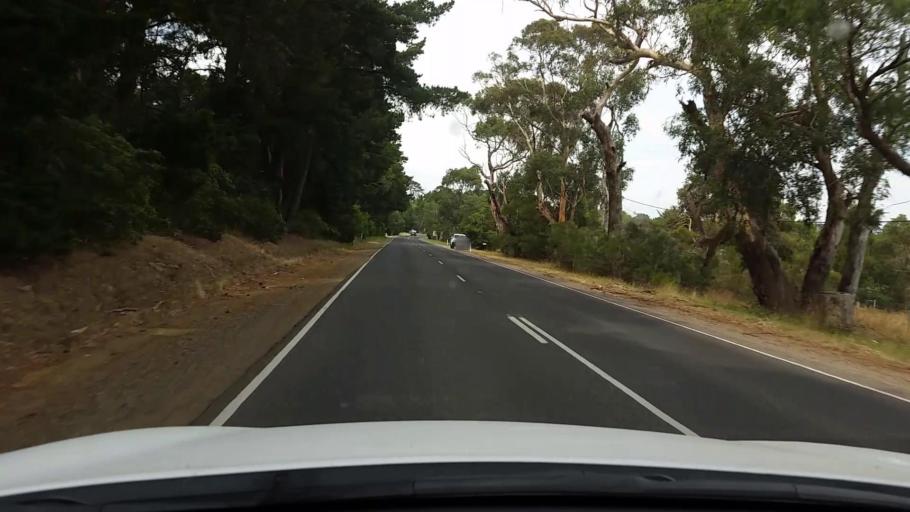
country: AU
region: Victoria
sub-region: Mornington Peninsula
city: Merricks
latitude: -38.3949
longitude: 145.0843
